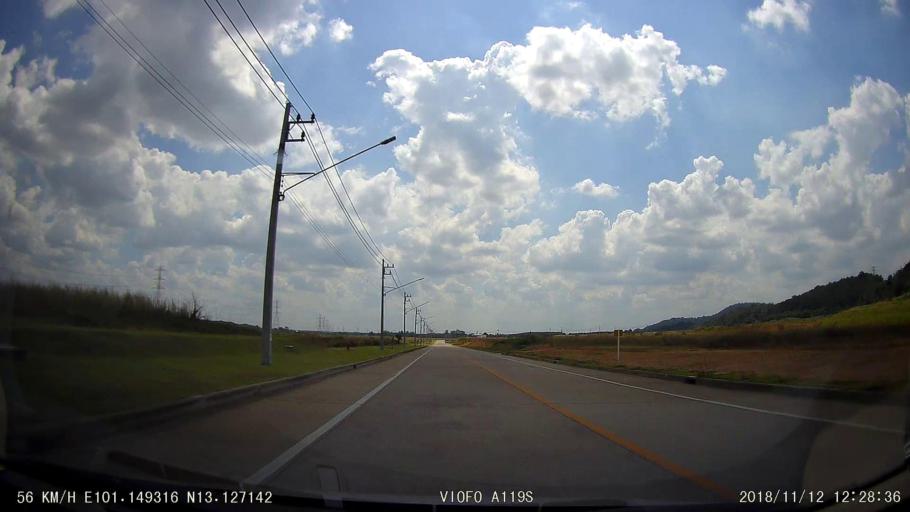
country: TH
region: Chon Buri
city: Ban Talat Bueng
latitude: 13.1265
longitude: 101.1493
